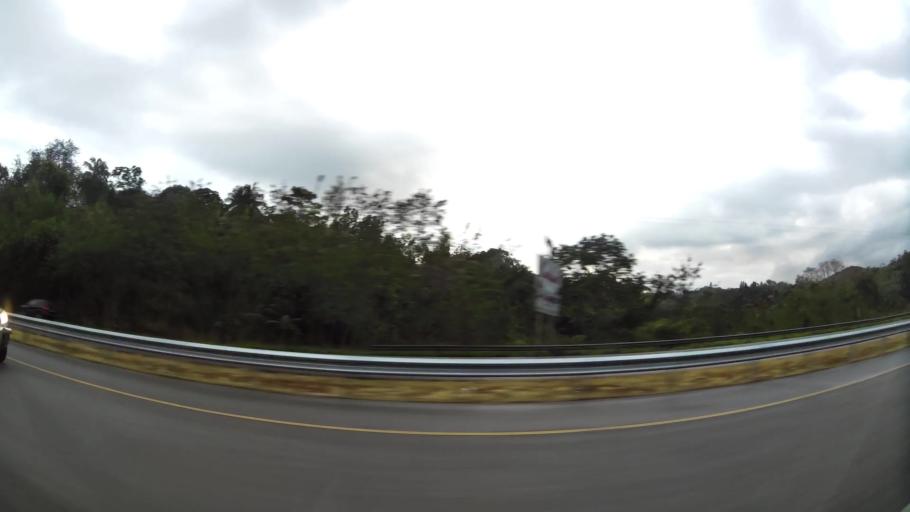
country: DO
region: San Cristobal
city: Villa Altagracia
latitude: 18.5814
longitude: -70.1118
